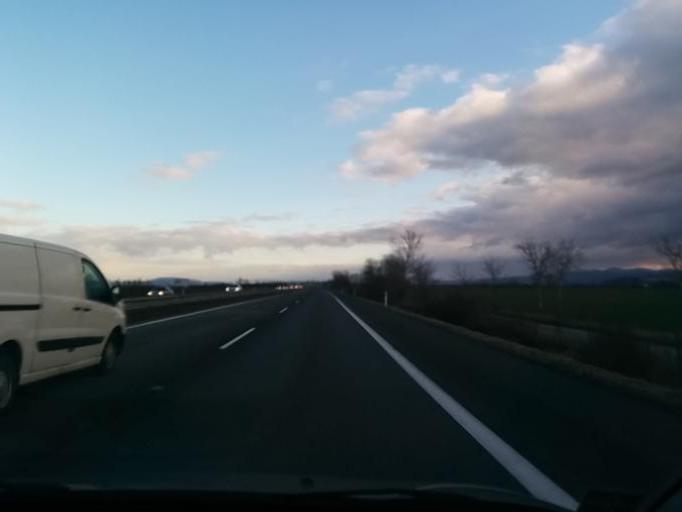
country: SK
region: Trnavsky
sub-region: Okres Trnava
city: Piestany
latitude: 48.5382
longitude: 17.7847
